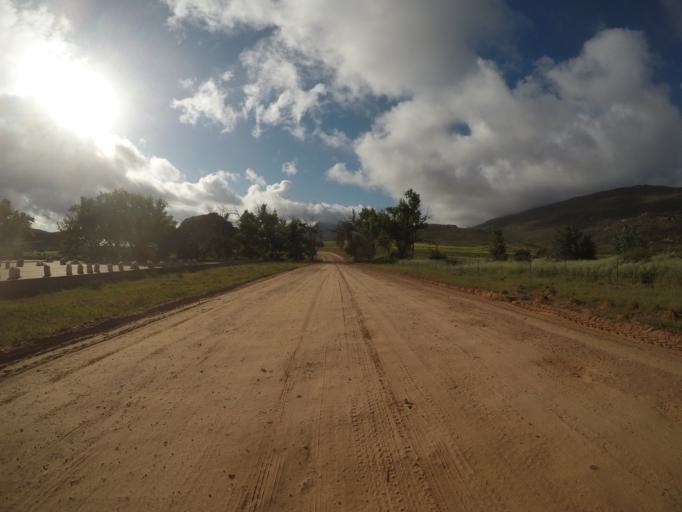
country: ZA
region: Western Cape
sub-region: West Coast District Municipality
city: Clanwilliam
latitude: -32.3428
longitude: 18.8334
